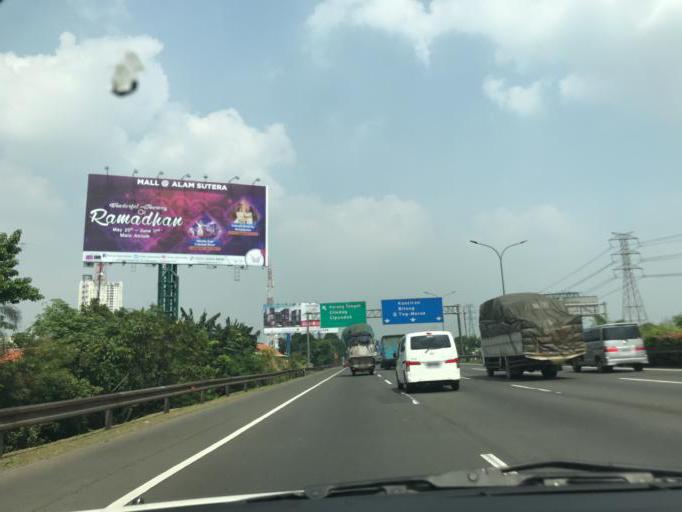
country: ID
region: West Java
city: Ciputat
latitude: -6.1989
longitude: 106.7104
